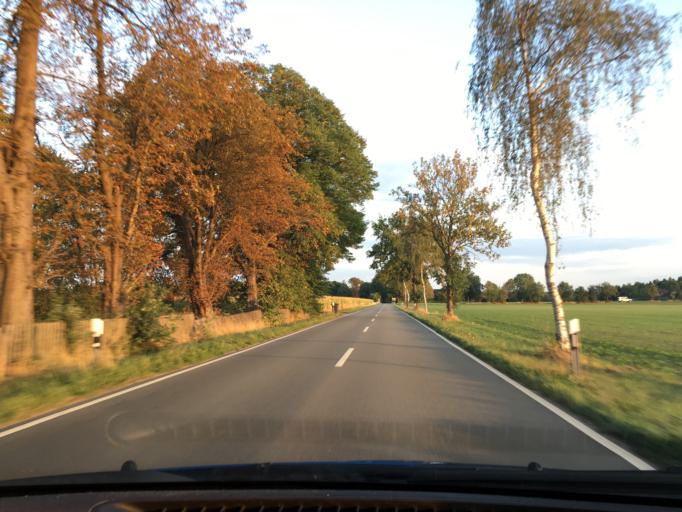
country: DE
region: Lower Saxony
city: Tosterglope
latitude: 53.2141
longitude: 10.8165
